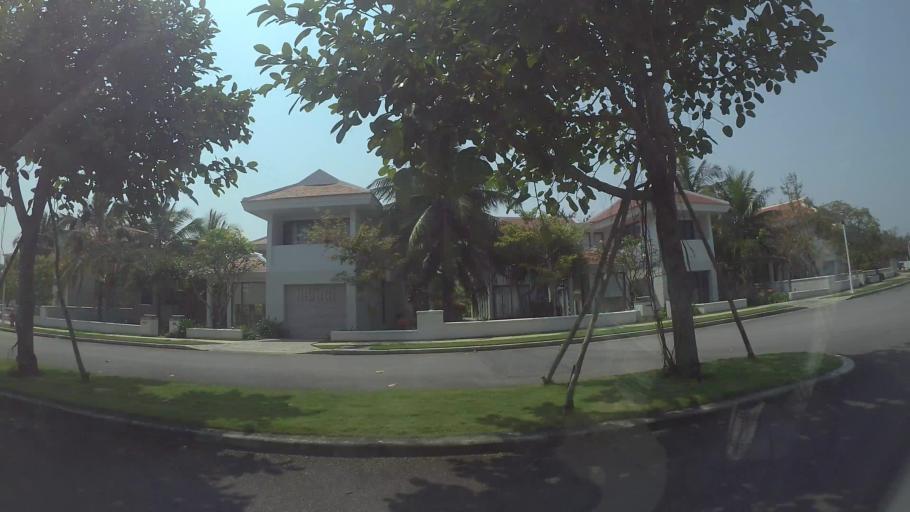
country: VN
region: Da Nang
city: Ngu Hanh Son
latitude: 15.9759
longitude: 108.2821
